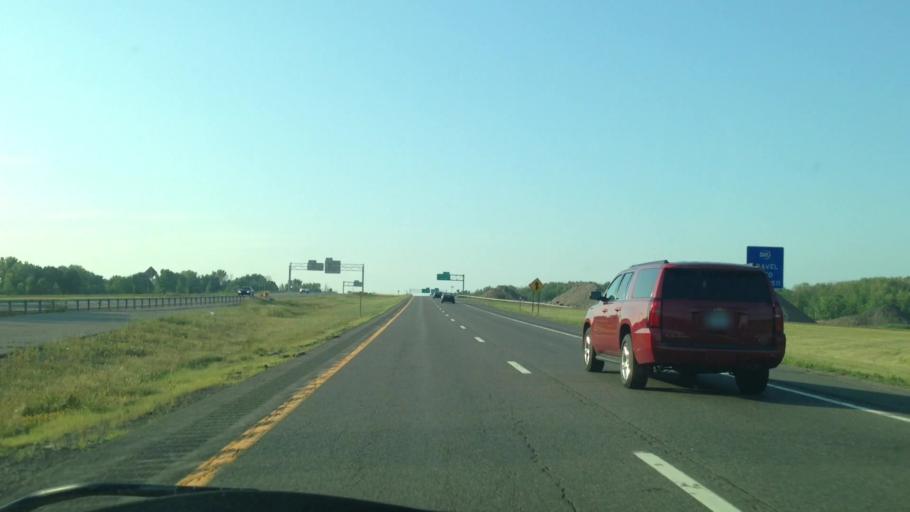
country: US
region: New York
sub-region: Onondaga County
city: East Syracuse
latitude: 43.0739
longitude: -76.0534
